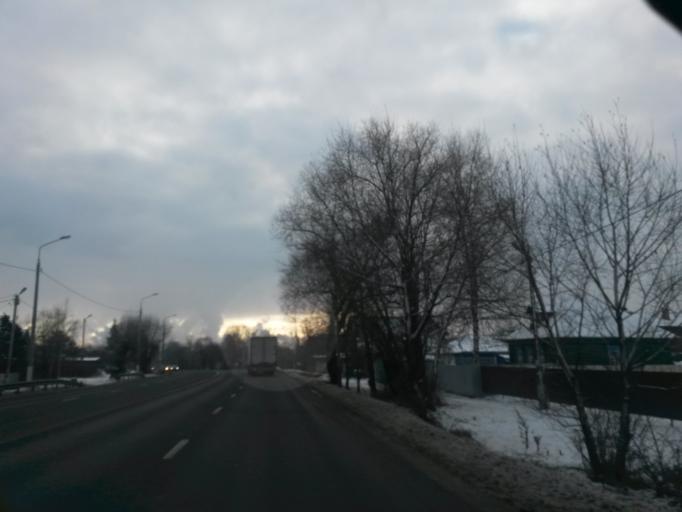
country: RU
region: Moskovskaya
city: Klimovsk
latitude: 55.3484
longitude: 37.5284
